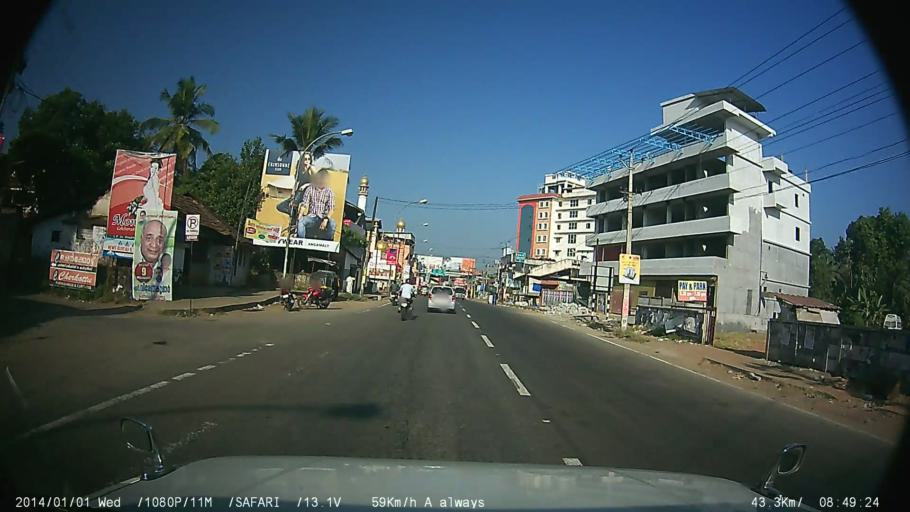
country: IN
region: Kerala
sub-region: Ernakulam
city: Angamali
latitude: 10.1889
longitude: 76.3917
